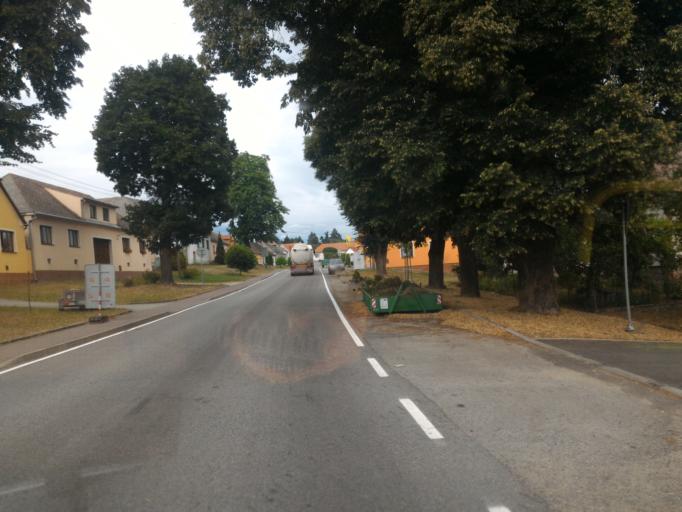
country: CZ
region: Vysocina
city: Zeletava
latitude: 49.1783
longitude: 15.5946
